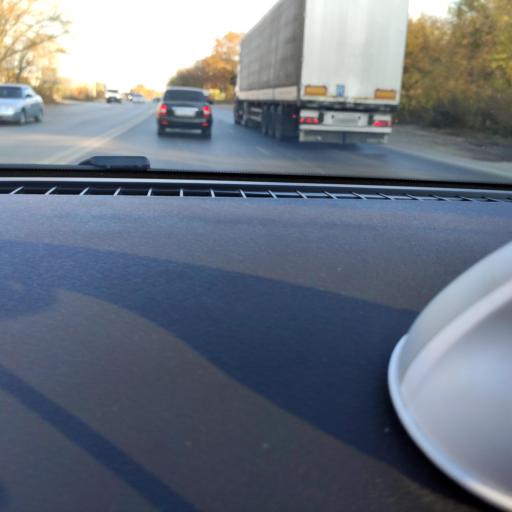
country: RU
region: Samara
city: Petra-Dubrava
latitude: 53.2739
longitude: 50.2666
